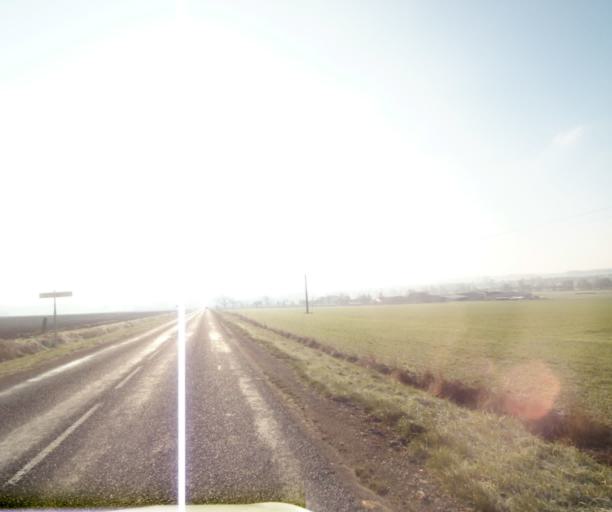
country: FR
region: Champagne-Ardenne
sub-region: Departement de la Haute-Marne
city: Montier-en-Der
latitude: 48.4941
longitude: 4.7549
